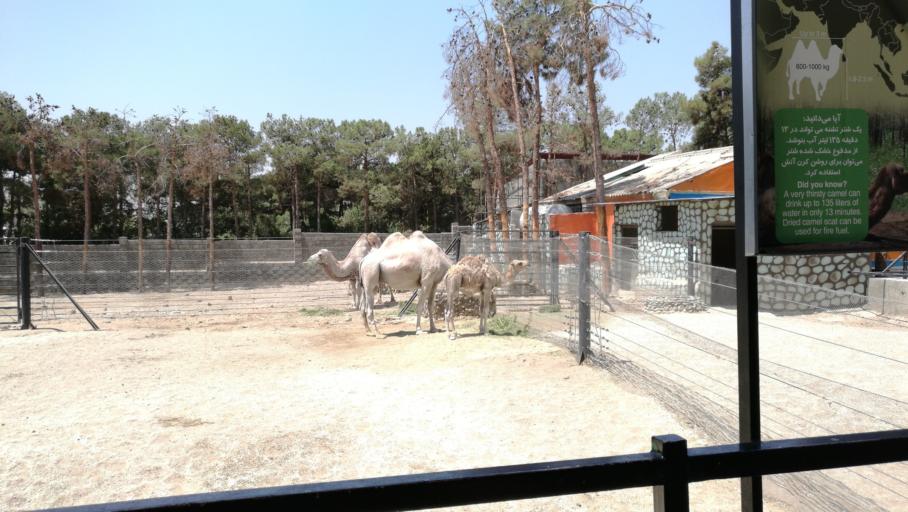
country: IR
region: Tehran
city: Tehran
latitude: 35.7185
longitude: 51.2927
